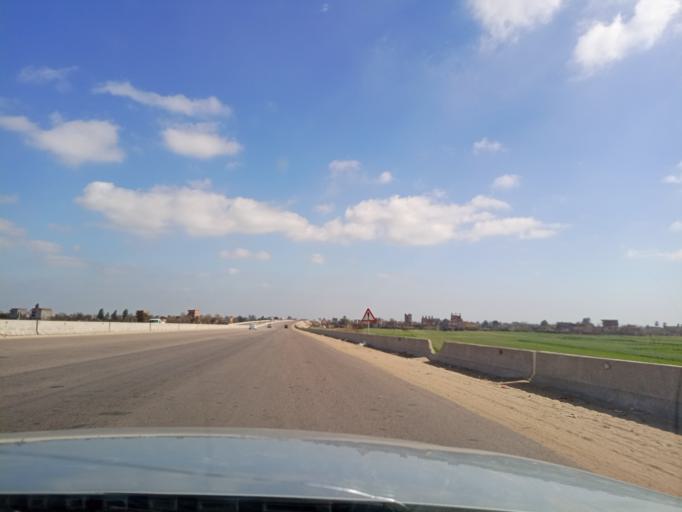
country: EG
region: Muhafazat al Minufiyah
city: Al Bajur
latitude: 30.3917
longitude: 30.9978
